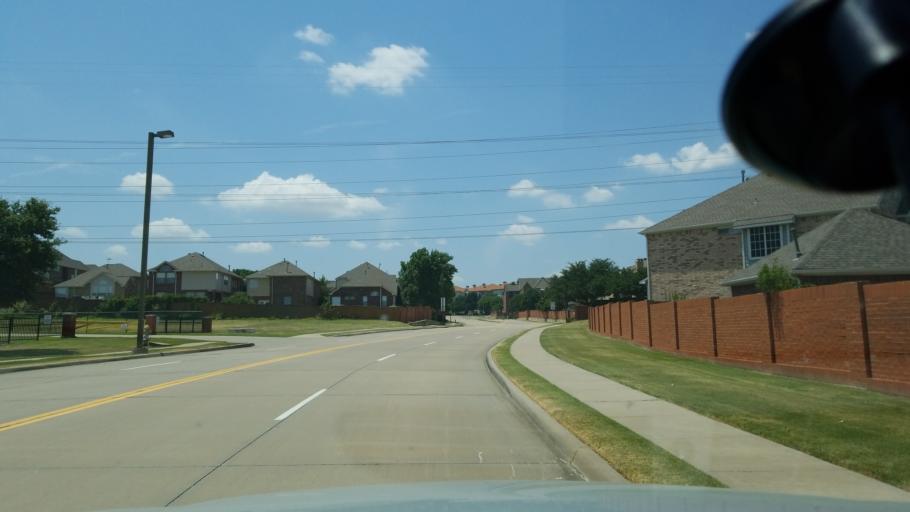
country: US
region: Texas
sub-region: Dallas County
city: Farmers Branch
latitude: 32.9198
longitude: -96.9498
